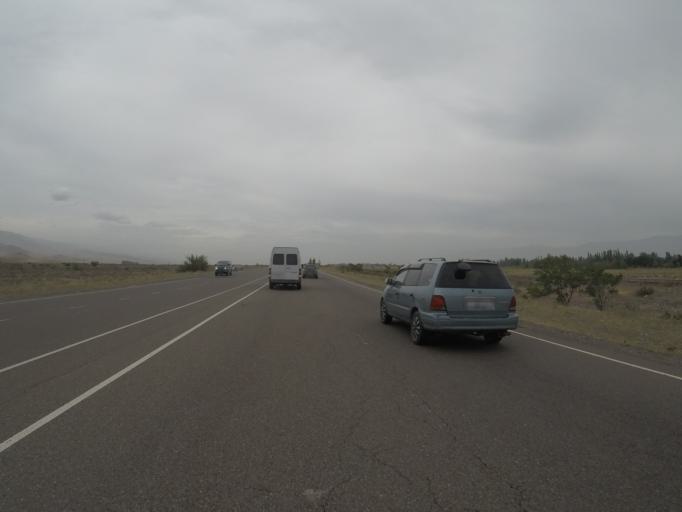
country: KG
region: Chuy
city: Bystrovka
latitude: 42.8292
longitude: 75.5271
